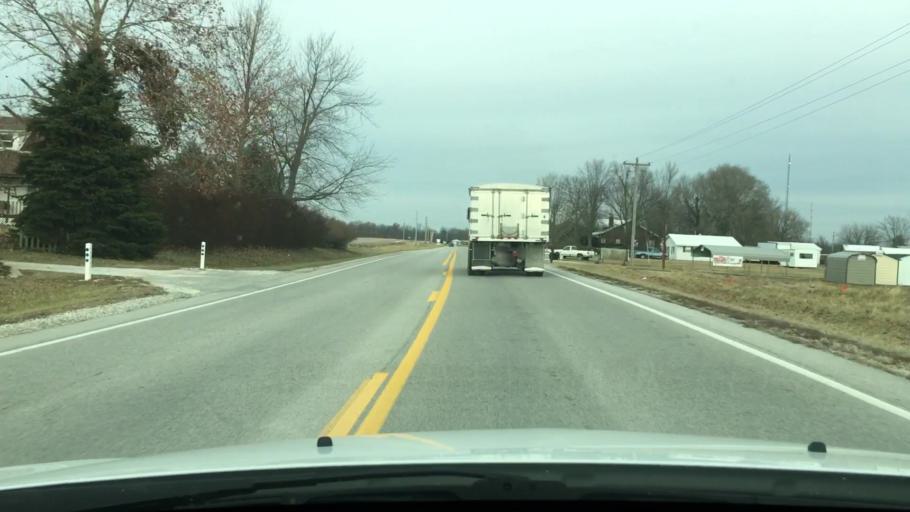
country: US
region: Illinois
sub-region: Pike County
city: Pittsfield
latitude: 39.6470
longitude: -90.7843
